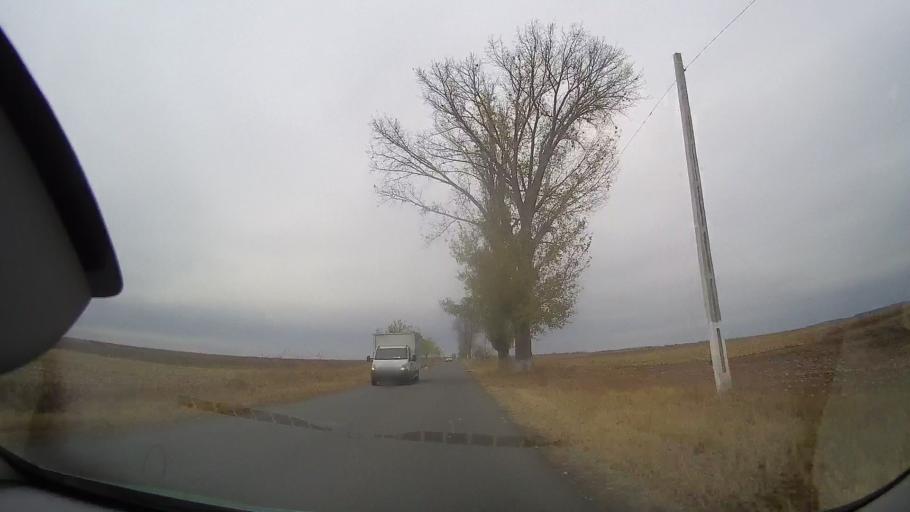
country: RO
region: Braila
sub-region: Comuna Budesti
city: Tataru
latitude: 44.8653
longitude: 27.4266
